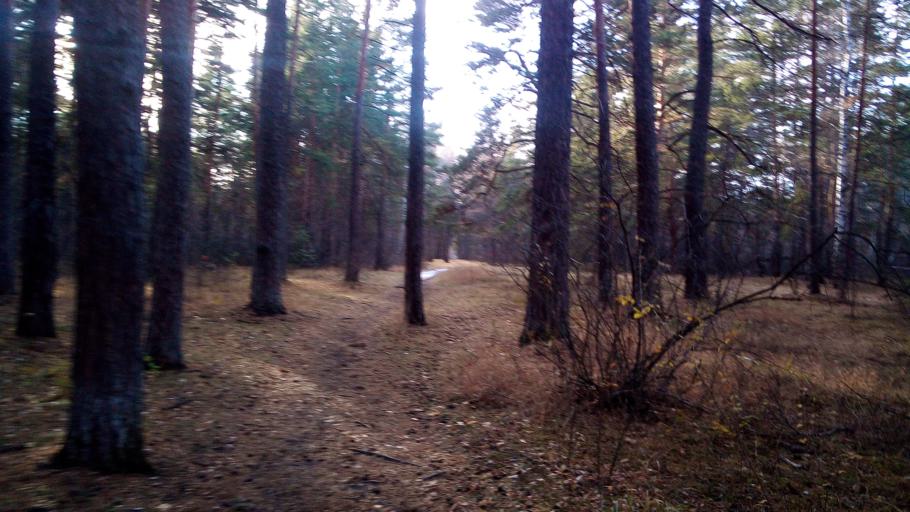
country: RU
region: Chelyabinsk
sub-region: Gorod Chelyabinsk
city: Chelyabinsk
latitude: 55.1565
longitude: 61.3571
